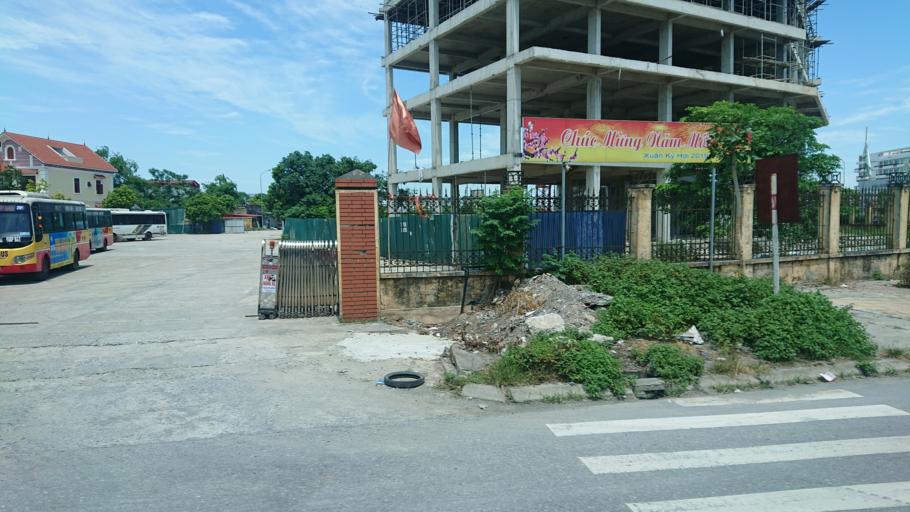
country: VN
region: Ha Nam
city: Thanh Pho Phu Ly
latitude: 20.5387
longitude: 105.9451
